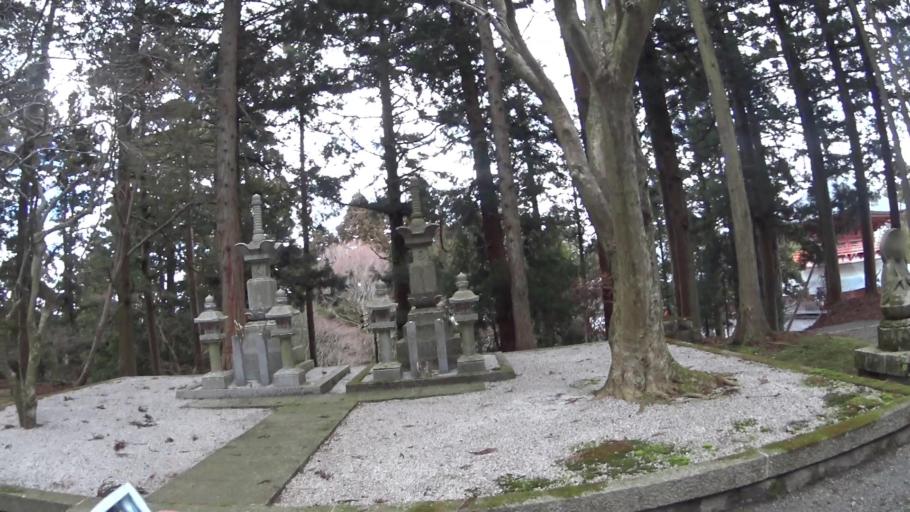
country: JP
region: Shiga Prefecture
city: Otsu-shi
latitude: 35.0706
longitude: 135.8370
